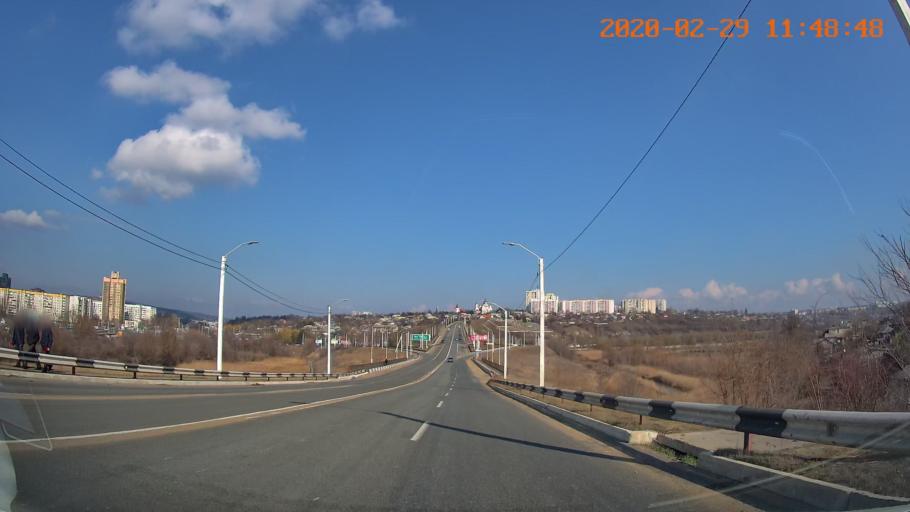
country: MD
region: Telenesti
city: Ribnita
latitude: 47.7504
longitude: 28.9924
